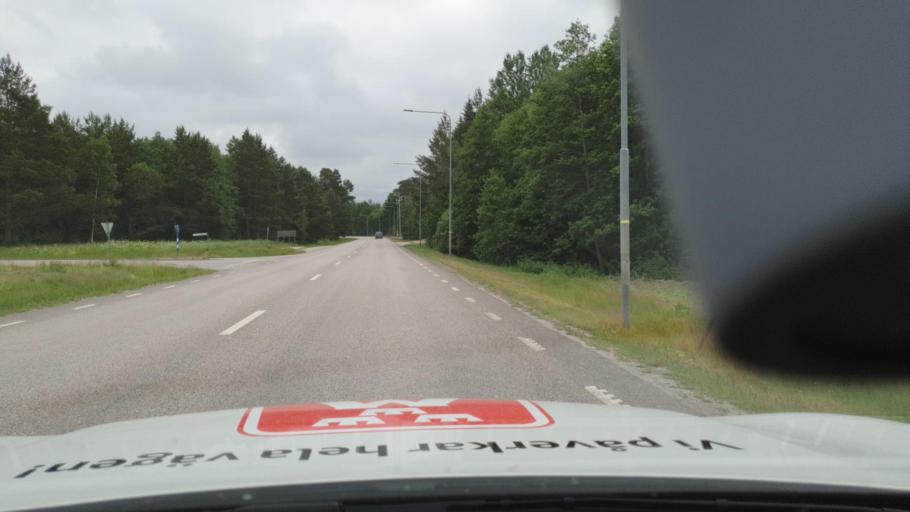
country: SE
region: Vaestra Goetaland
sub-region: Tibro Kommun
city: Tibro
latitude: 58.4126
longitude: 14.1655
